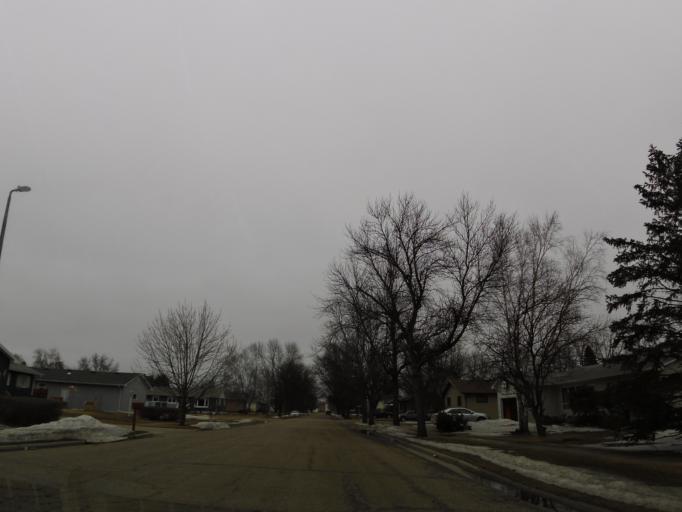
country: US
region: North Dakota
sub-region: Walsh County
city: Grafton
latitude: 48.4078
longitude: -97.4096
